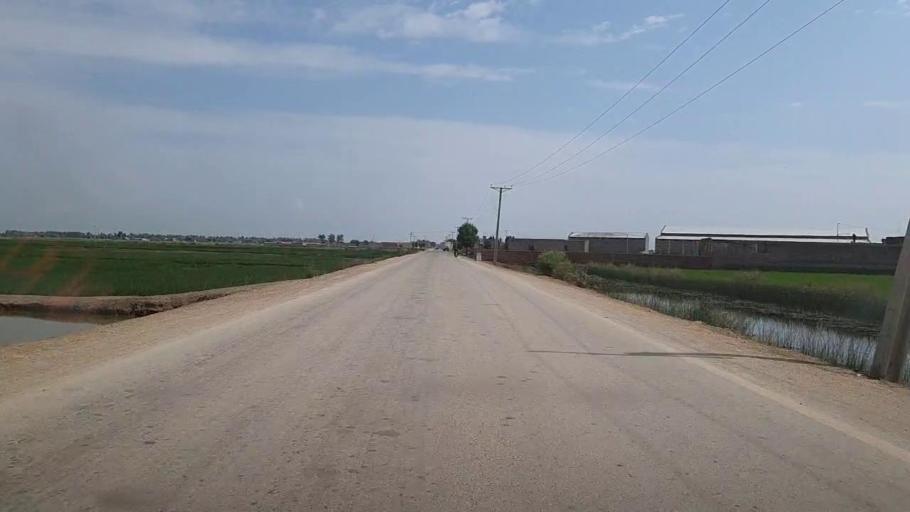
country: PK
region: Sindh
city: Thul
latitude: 28.2545
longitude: 68.7799
